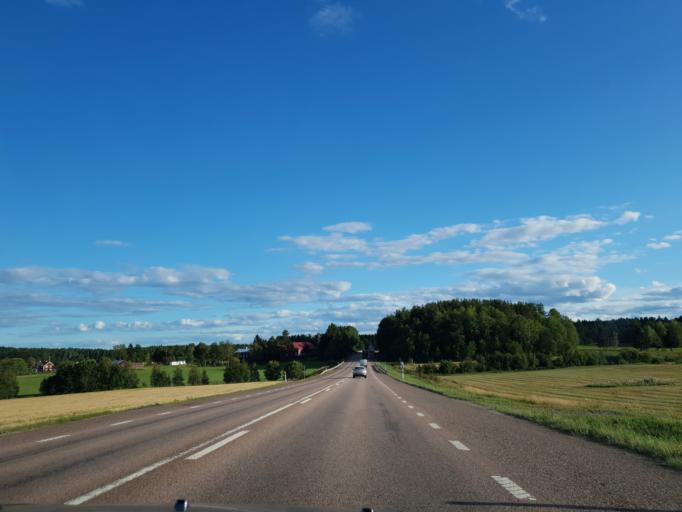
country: SE
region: Gaevleborg
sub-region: Nordanstigs Kommun
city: Bergsjoe
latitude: 61.9676
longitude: 17.2415
